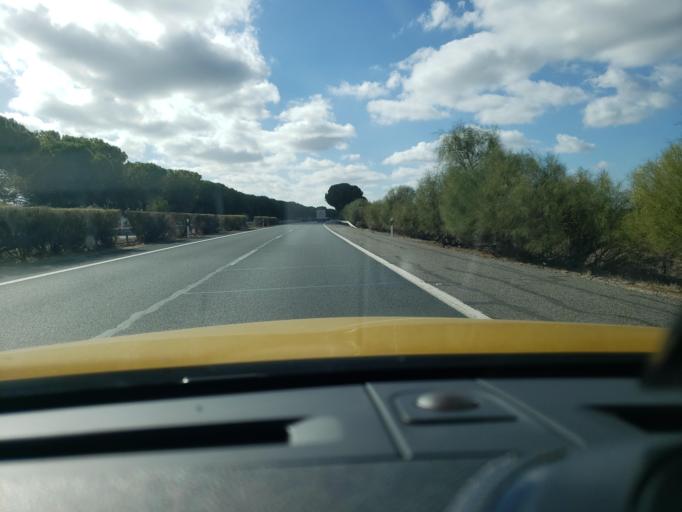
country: ES
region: Andalusia
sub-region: Provincia de Sevilla
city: Las Cabezas de San Juan
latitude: 36.8937
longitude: -5.9750
